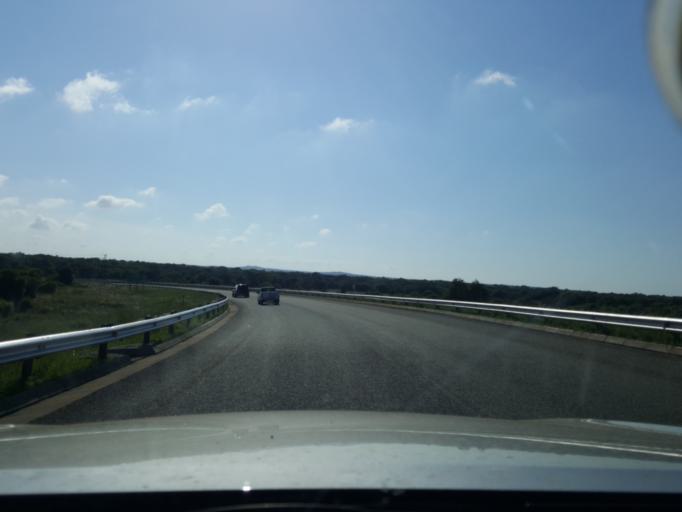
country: ZA
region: North-West
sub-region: Ngaka Modiri Molema District Municipality
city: Zeerust
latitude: -25.7548
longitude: 25.9629
